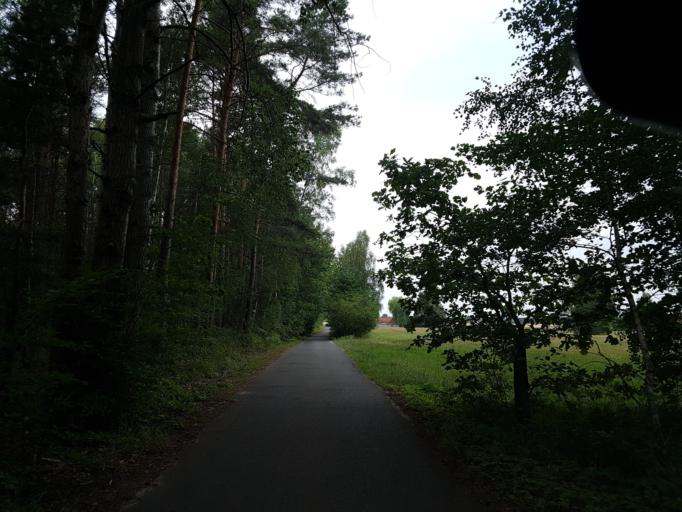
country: DE
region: Brandenburg
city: Sallgast
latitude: 51.5800
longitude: 13.8586
